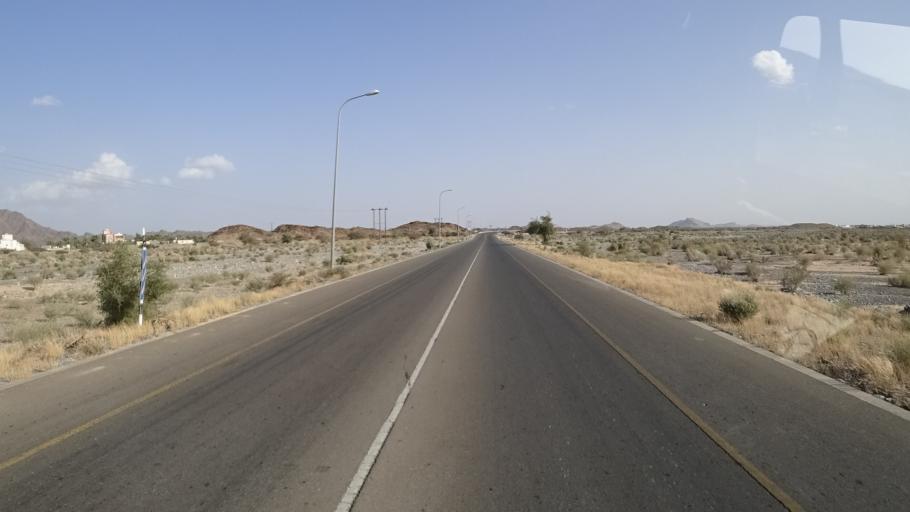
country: OM
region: Muhafazat ad Dakhiliyah
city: Izki
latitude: 22.8777
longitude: 57.7563
